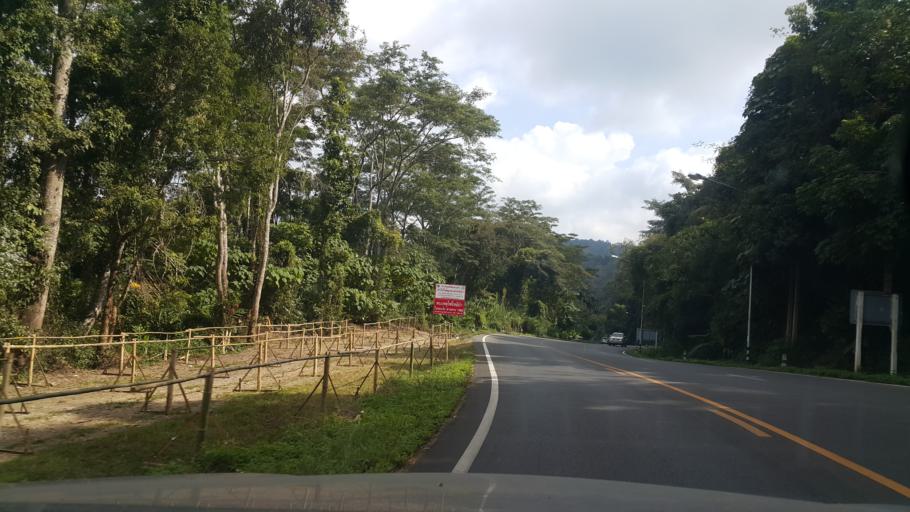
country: TH
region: Phayao
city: Phayao
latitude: 19.0606
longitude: 99.7829
